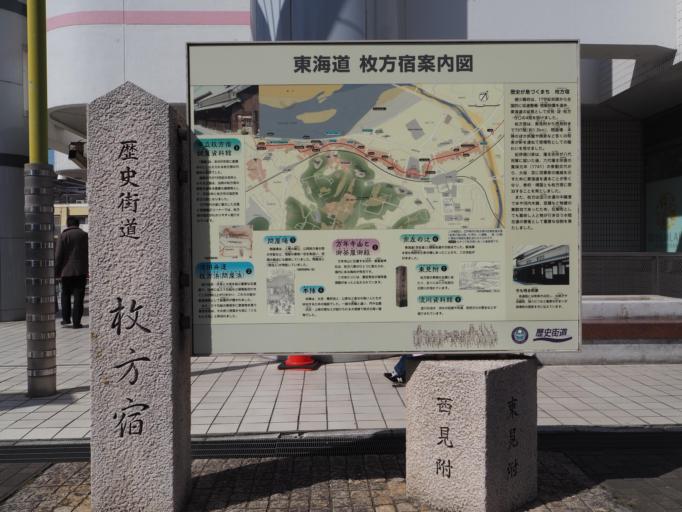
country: JP
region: Osaka
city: Hirakata
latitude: 34.8151
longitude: 135.6465
